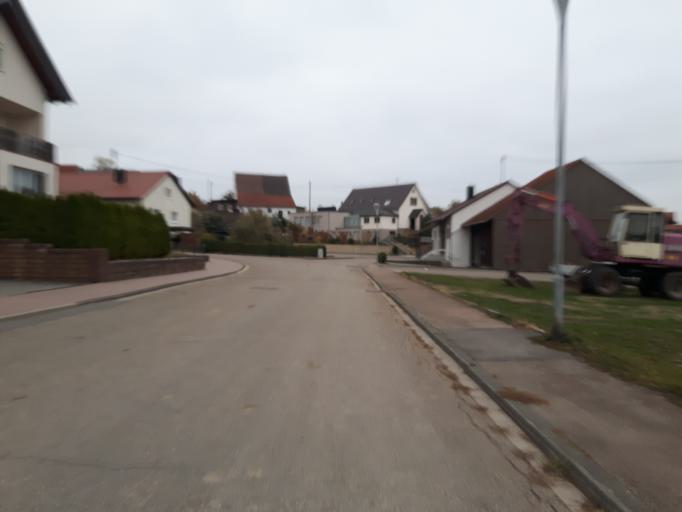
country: DE
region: Baden-Wuerttemberg
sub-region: Regierungsbezirk Stuttgart
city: Eppingen
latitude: 49.1713
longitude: 8.8914
